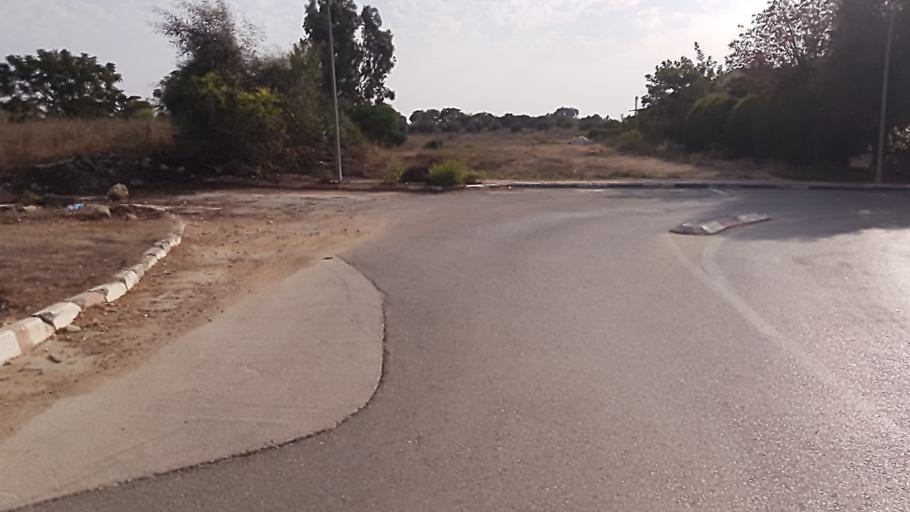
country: IL
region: Central District
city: Rosh Ha'Ayin
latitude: 32.0803
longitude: 34.9377
